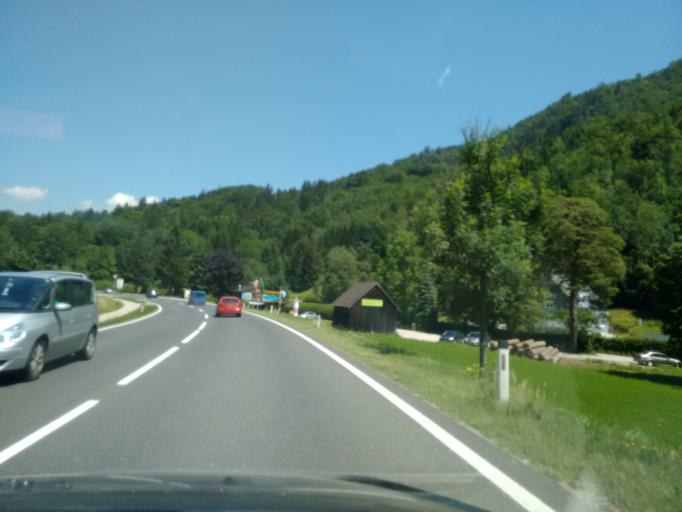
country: AT
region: Upper Austria
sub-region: Politischer Bezirk Gmunden
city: Bad Ischl
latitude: 47.6854
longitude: 13.6257
